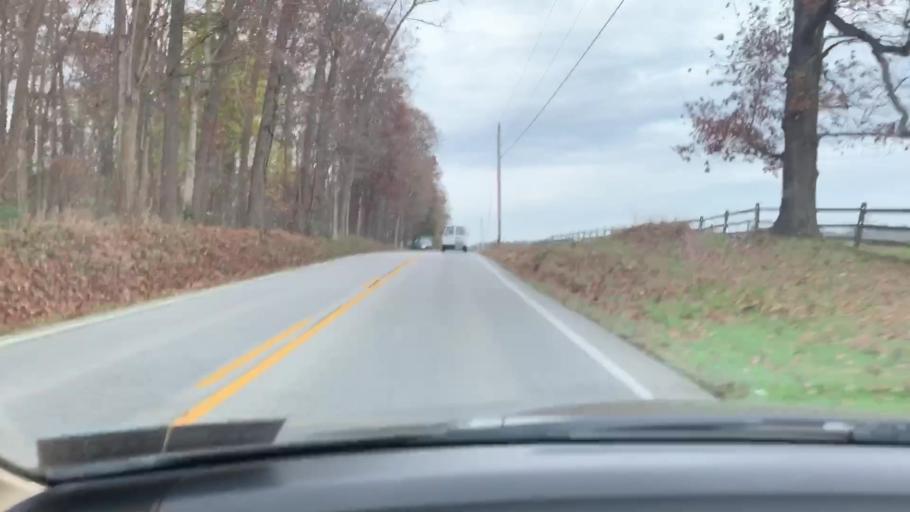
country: US
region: Pennsylvania
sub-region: Adams County
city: Lake Meade
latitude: 39.9429
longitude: -77.0778
